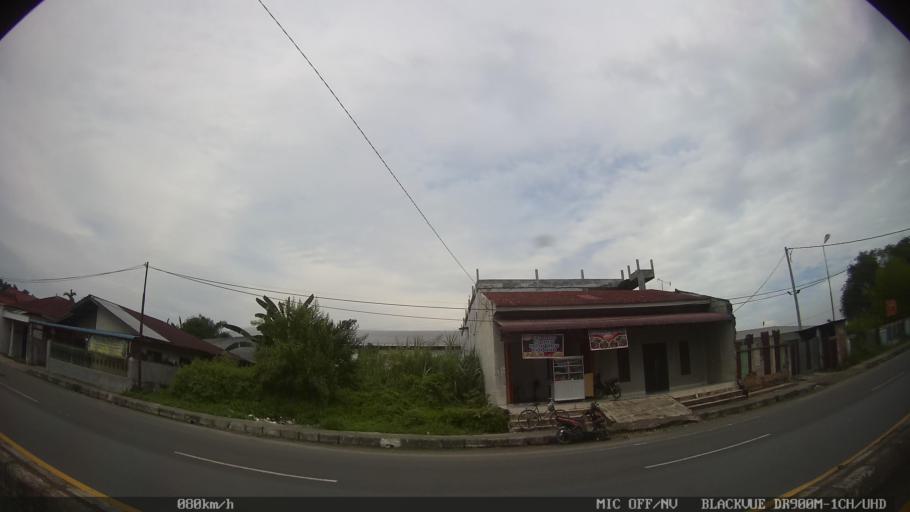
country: ID
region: North Sumatra
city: Sunggal
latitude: 3.6121
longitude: 98.5758
